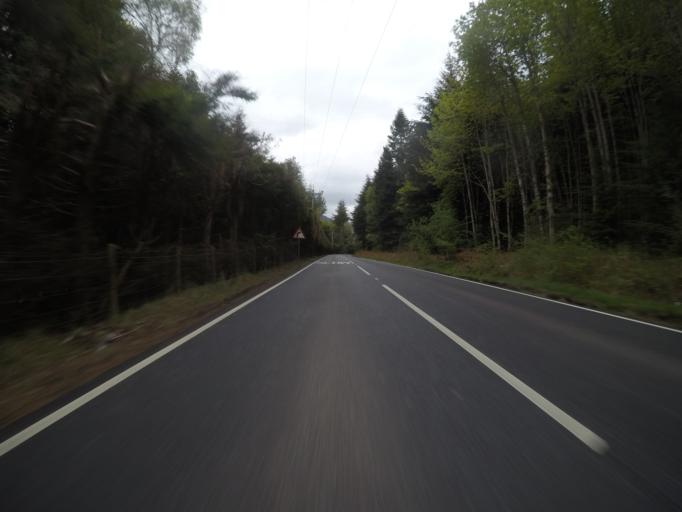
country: GB
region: Scotland
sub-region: Highland
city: Beauly
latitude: 57.1888
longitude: -4.6192
